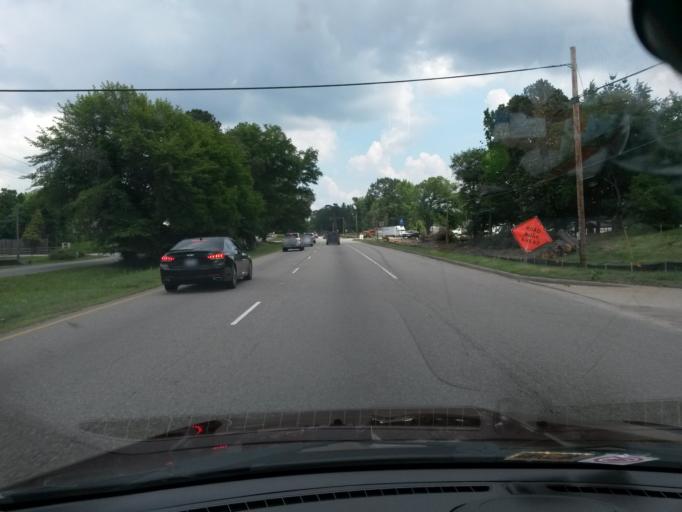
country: US
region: Virginia
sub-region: Chesterfield County
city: Chester
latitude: 37.3502
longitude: -77.3824
